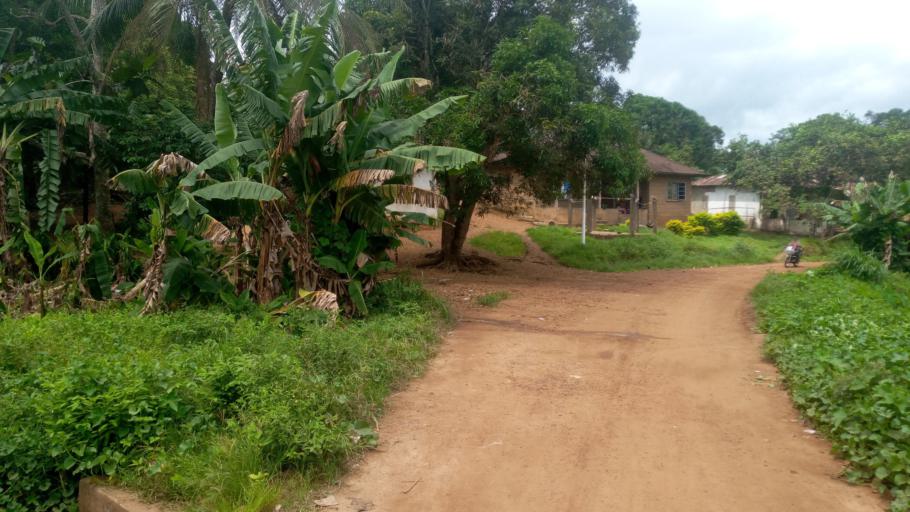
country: SL
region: Southern Province
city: Mogbwemo
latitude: 7.6048
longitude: -12.1756
